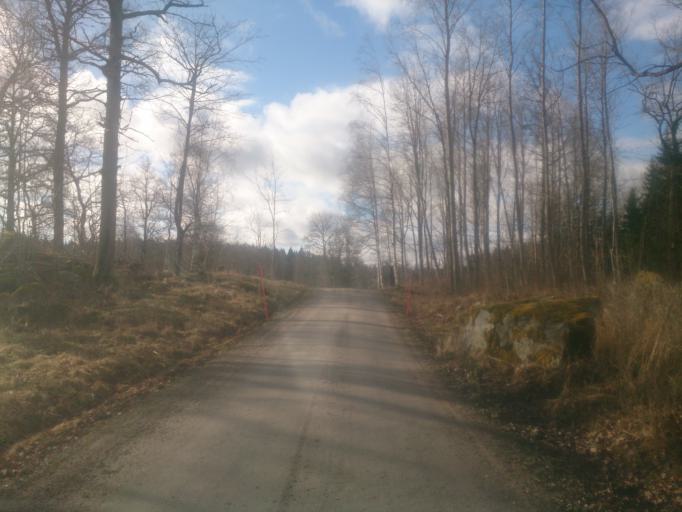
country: SE
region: OEstergoetland
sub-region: Atvidabergs Kommun
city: Atvidaberg
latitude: 58.2315
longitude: 16.1791
